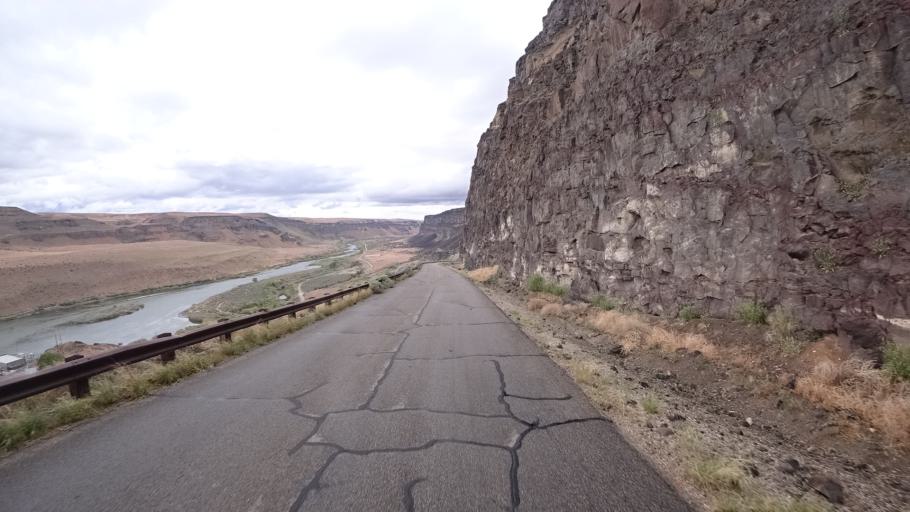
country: US
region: Idaho
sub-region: Owyhee County
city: Murphy
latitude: 43.2446
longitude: -116.3725
